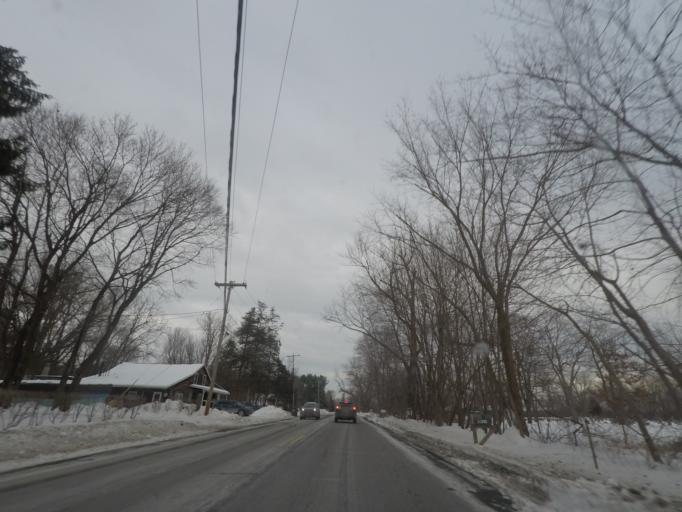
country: US
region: New York
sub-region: Greene County
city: Coxsackie
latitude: 42.3499
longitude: -73.7449
